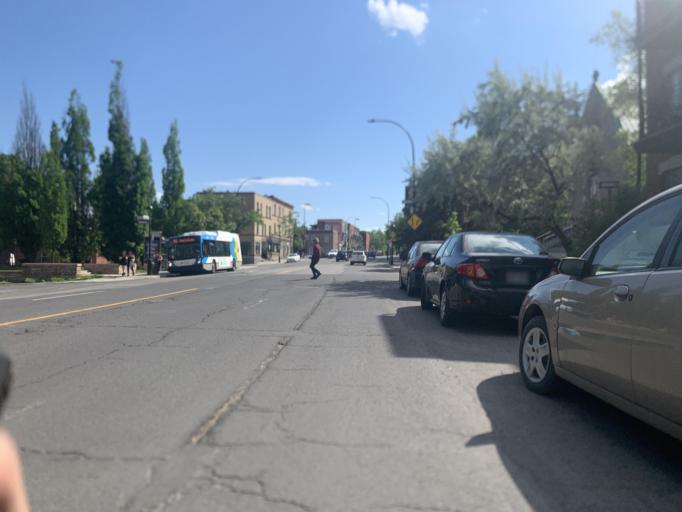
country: CA
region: Quebec
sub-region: Monteregie
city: Longueuil
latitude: 45.5365
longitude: -73.5579
